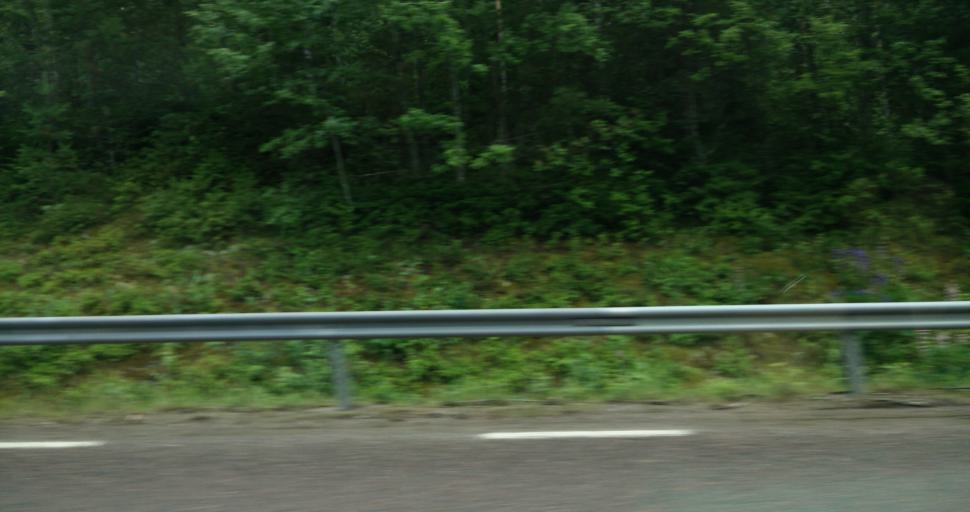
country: SE
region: Vaermland
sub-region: Munkfors Kommun
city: Munkfors
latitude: 59.9688
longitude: 13.5436
